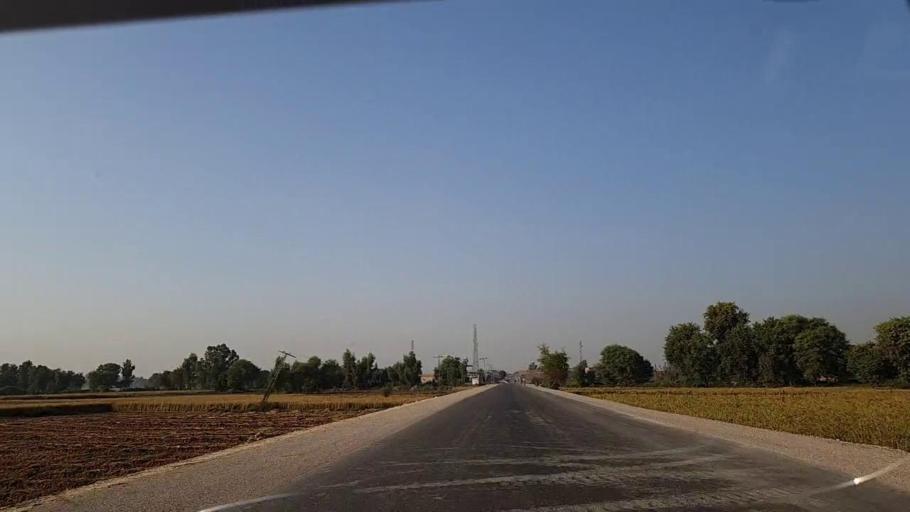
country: PK
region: Sindh
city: Rustam jo Goth
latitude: 27.9585
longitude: 68.8070
